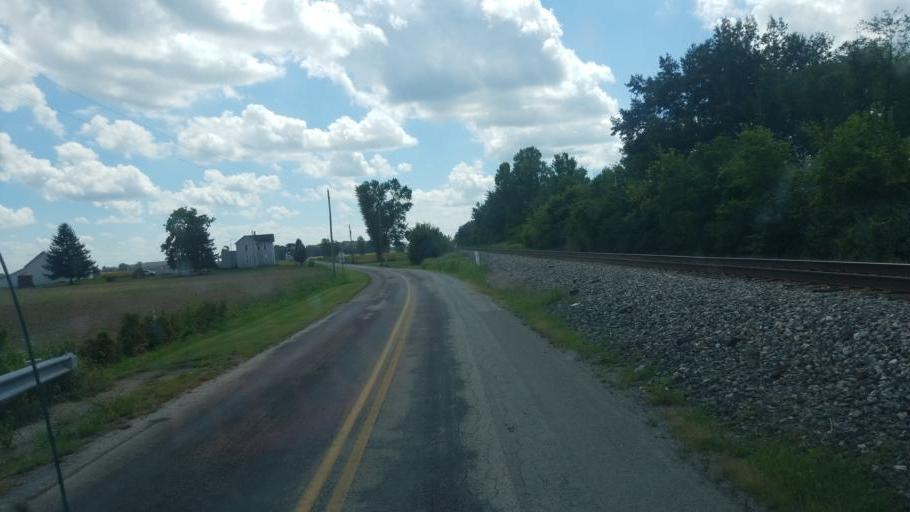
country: US
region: Ohio
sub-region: Marion County
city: Prospect
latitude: 40.4906
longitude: -83.1662
